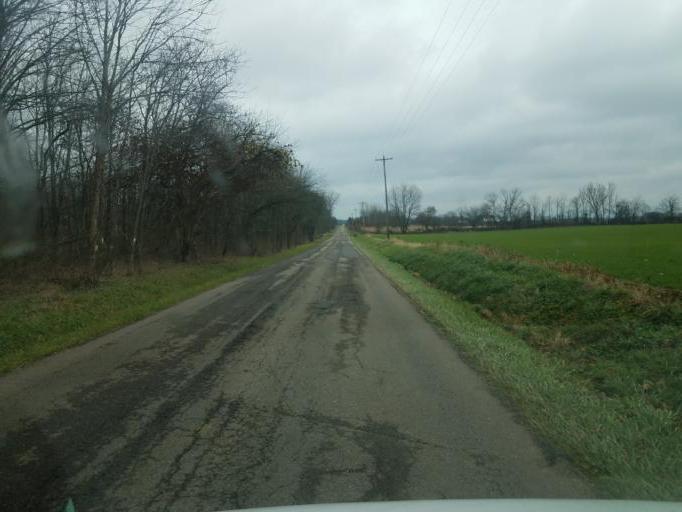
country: US
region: Ohio
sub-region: Knox County
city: Centerburg
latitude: 40.3186
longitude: -82.6180
